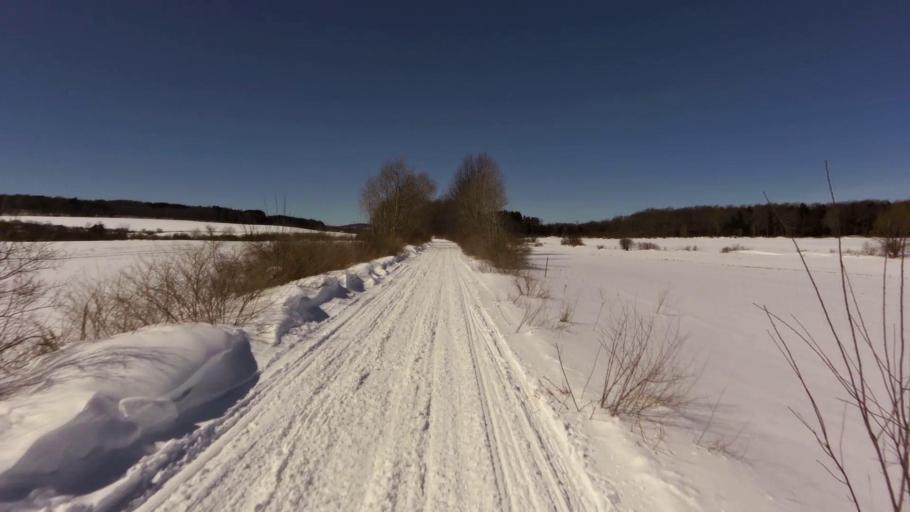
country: US
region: New York
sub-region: Cattaraugus County
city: Delevan
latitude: 42.4308
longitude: -78.3933
